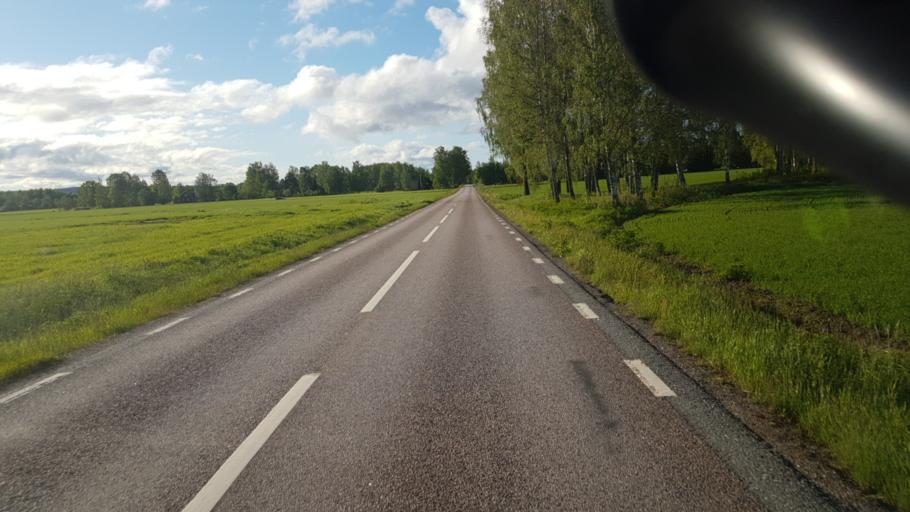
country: SE
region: Vaermland
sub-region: Arvika Kommun
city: Arvika
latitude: 59.6112
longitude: 12.5225
